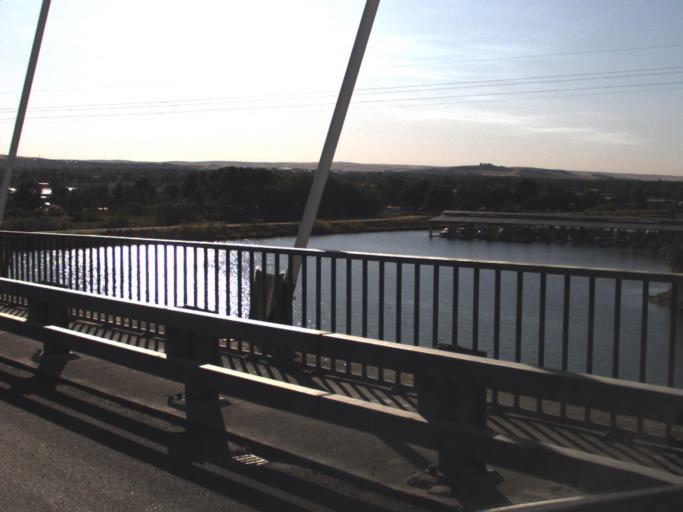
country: US
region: Washington
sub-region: Franklin County
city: Pasco
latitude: 46.2175
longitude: -119.1053
